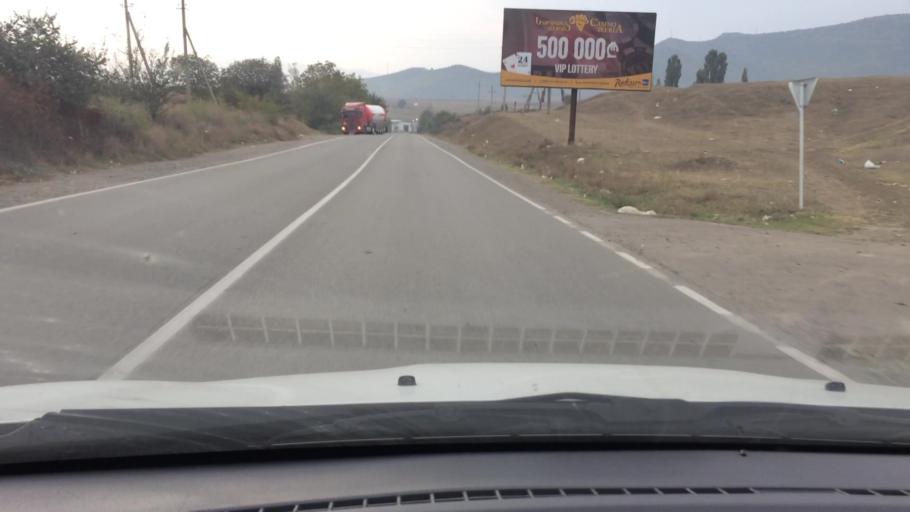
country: AM
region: Tavush
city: Bagratashen
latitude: 41.2304
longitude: 44.8203
